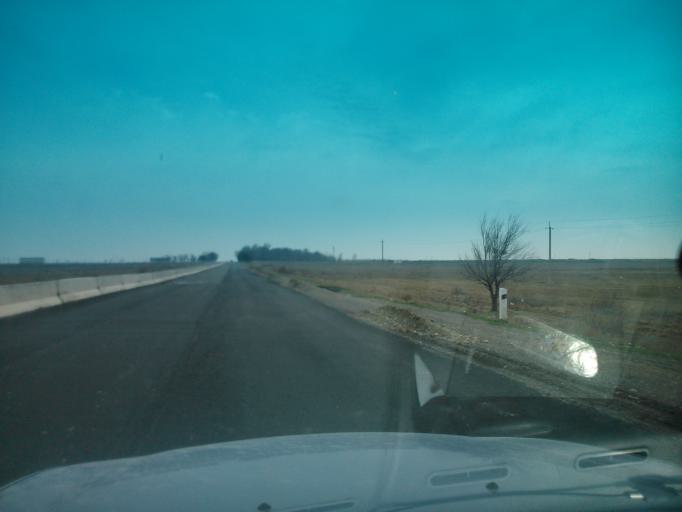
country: UZ
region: Sirdaryo
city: Yangiyer
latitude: 40.3381
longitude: 68.8094
